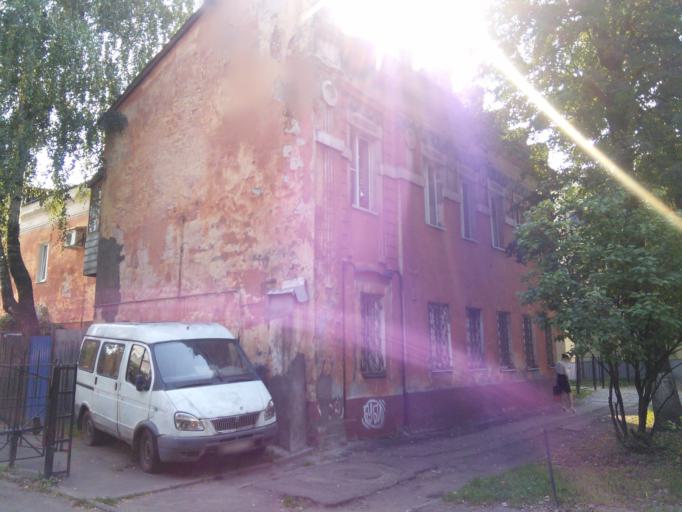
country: RU
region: Jaroslavl
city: Yaroslavl
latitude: 57.6376
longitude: 39.8880
